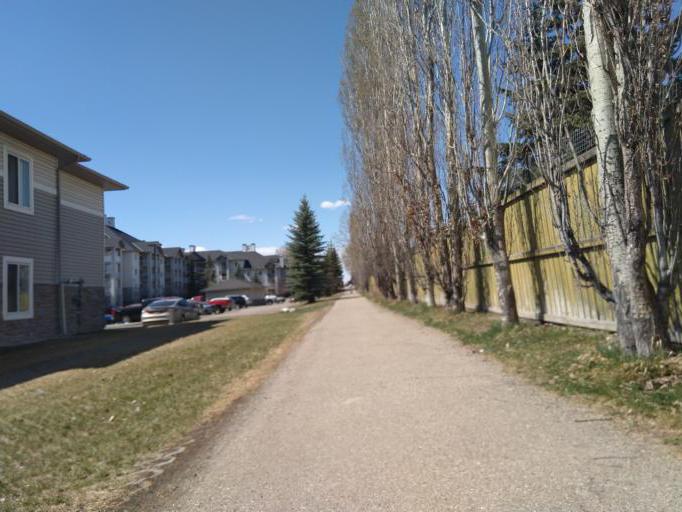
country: CA
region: Alberta
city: Chestermere
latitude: 51.0397
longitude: -113.9278
